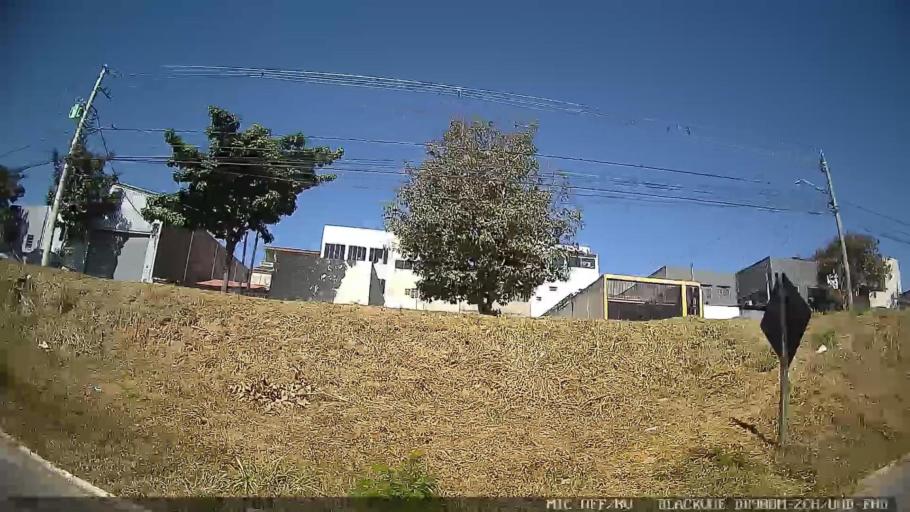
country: BR
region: Sao Paulo
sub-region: Jacarei
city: Jacarei
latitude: -23.2629
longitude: -45.9274
